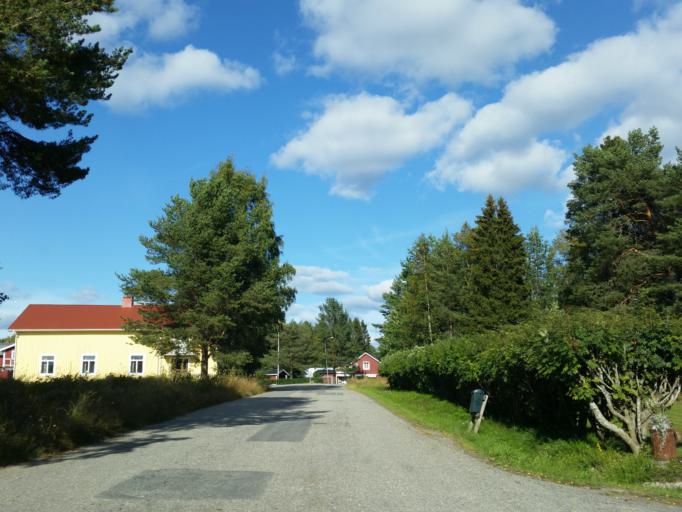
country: SE
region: Vaesterbotten
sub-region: Robertsfors Kommun
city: Robertsfors
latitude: 64.1699
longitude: 20.9382
